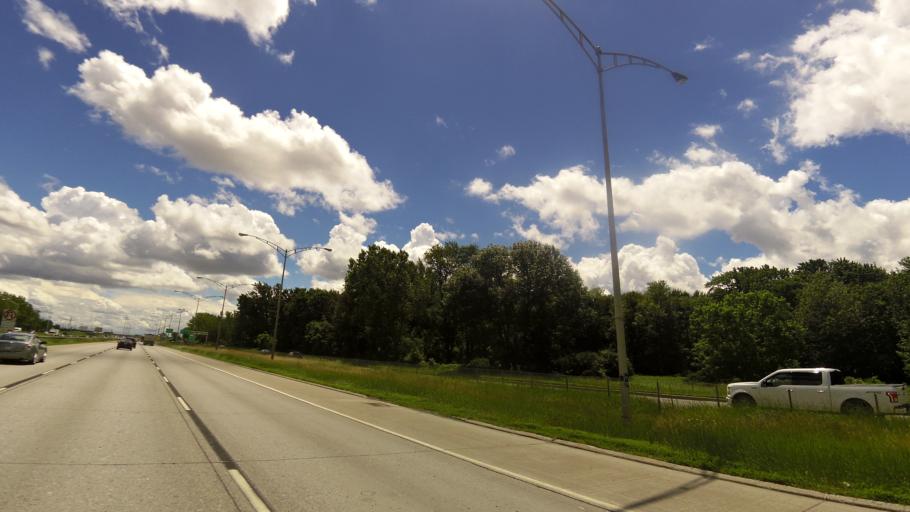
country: CA
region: Quebec
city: Dollard-Des Ormeaux
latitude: 45.5489
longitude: -73.8032
